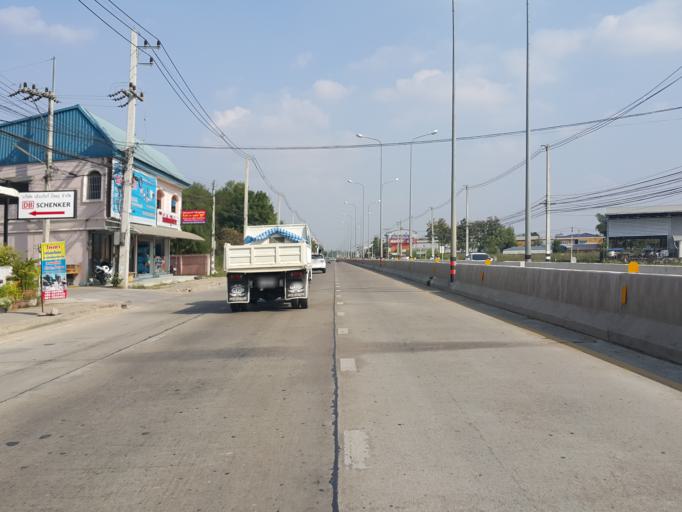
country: TH
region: Chiang Mai
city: Chiang Mai
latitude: 18.7411
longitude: 98.9658
